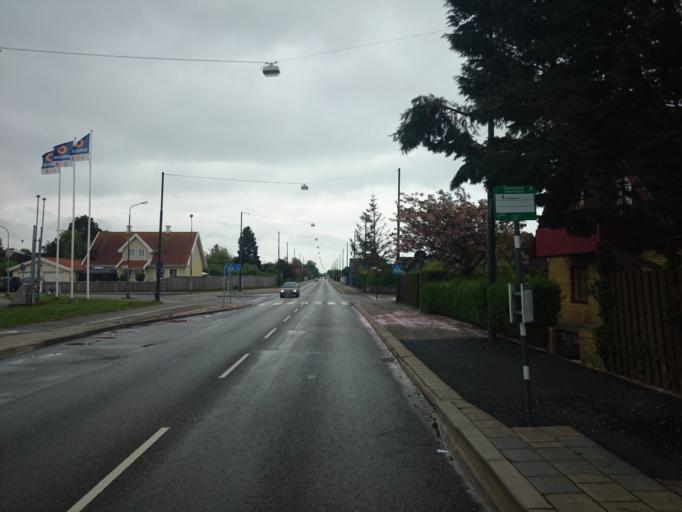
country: SE
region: Skane
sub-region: Malmo
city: Bunkeflostrand
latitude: 55.5607
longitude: 12.9193
